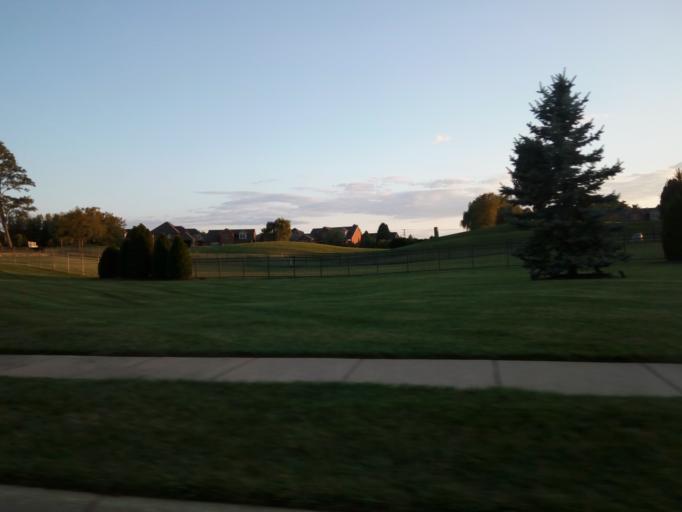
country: US
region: Kentucky
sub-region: Oldham County
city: Pewee Valley
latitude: 38.2732
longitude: -85.4817
